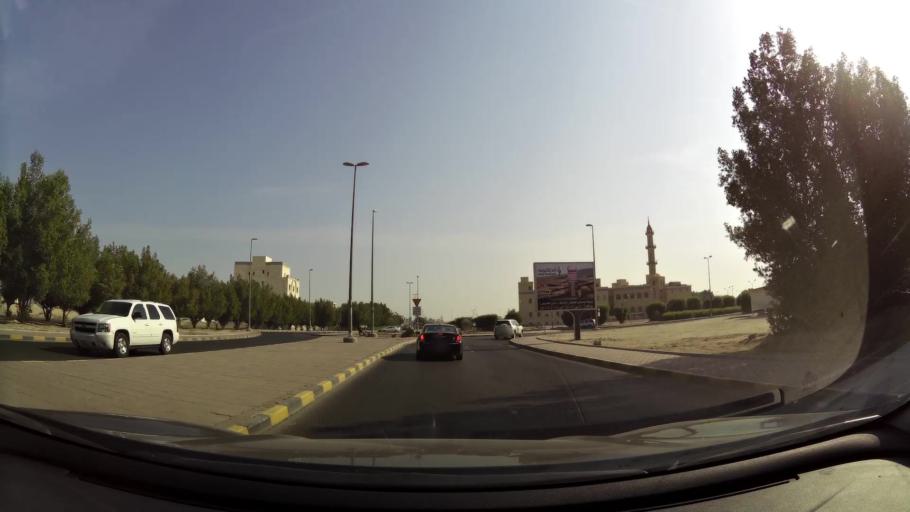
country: KW
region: Mubarak al Kabir
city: Mubarak al Kabir
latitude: 29.1880
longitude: 48.0998
